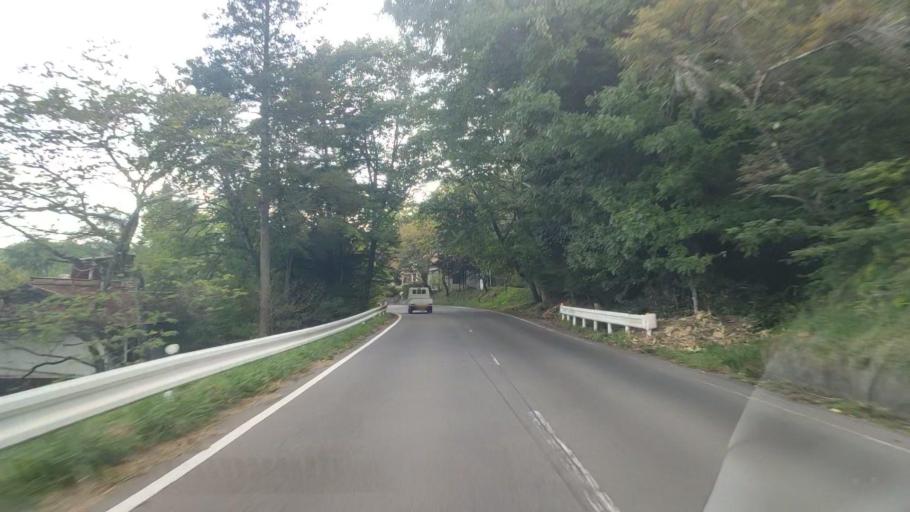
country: JP
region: Nagano
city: Suzaka
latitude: 36.5843
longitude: 138.5703
